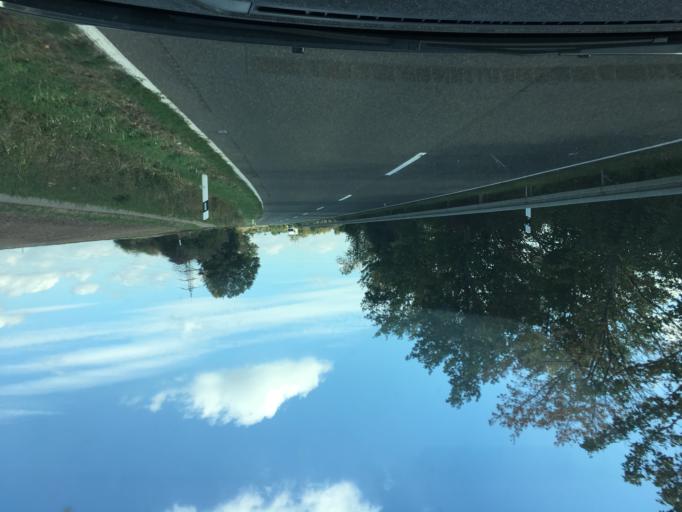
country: DE
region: North Rhine-Westphalia
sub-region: Regierungsbezirk Koln
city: Nideggen
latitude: 50.6855
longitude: 6.5005
